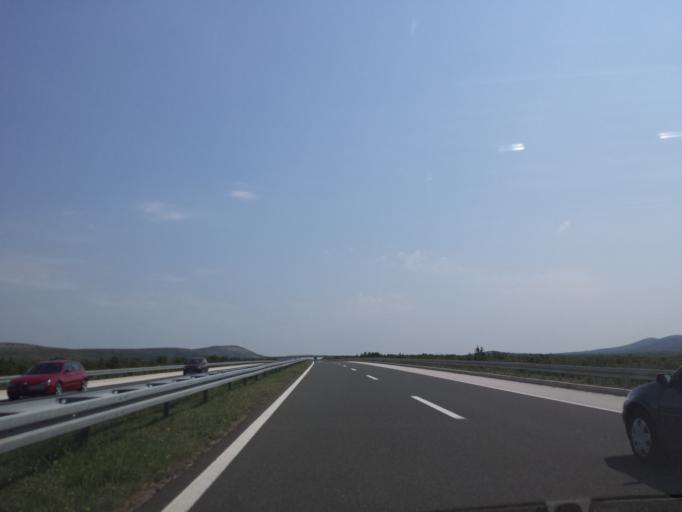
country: HR
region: Zadarska
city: Benkovac
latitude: 43.9591
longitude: 15.6674
